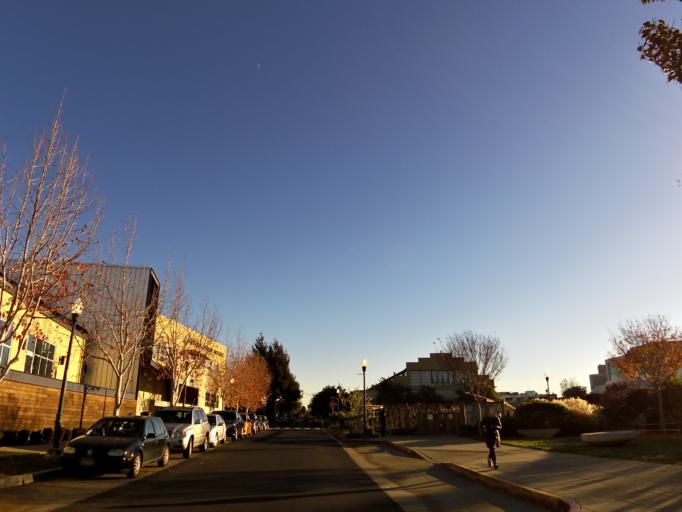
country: US
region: California
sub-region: Alameda County
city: Emeryville
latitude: 37.8423
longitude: -122.2882
